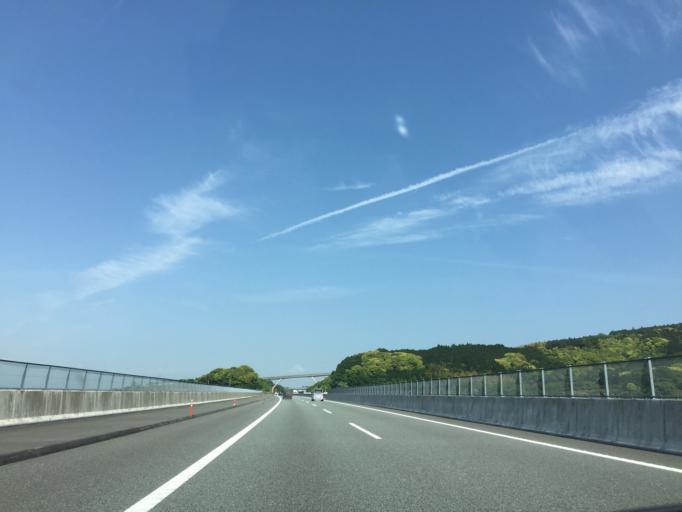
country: JP
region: Shizuoka
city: Fuji
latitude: 35.1732
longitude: 138.7435
